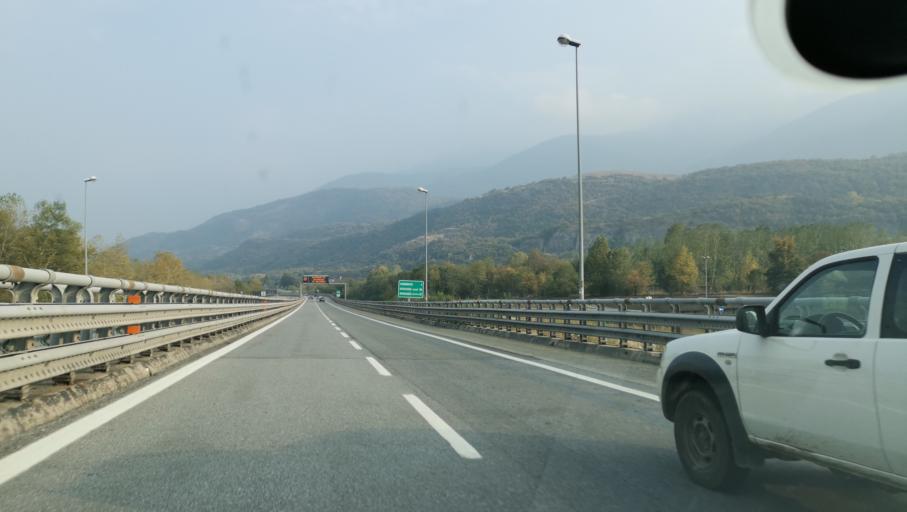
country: IT
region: Piedmont
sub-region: Provincia di Torino
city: Mattie
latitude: 45.1356
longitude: 7.0935
